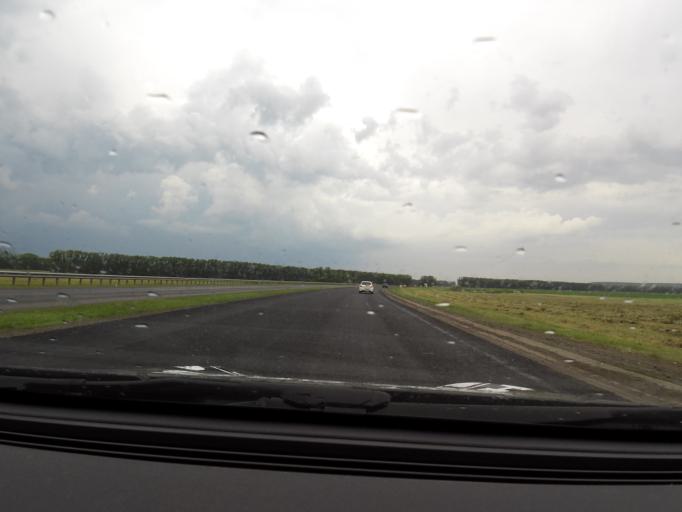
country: RU
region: Bashkortostan
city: Asanovo
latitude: 54.9270
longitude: 55.5769
